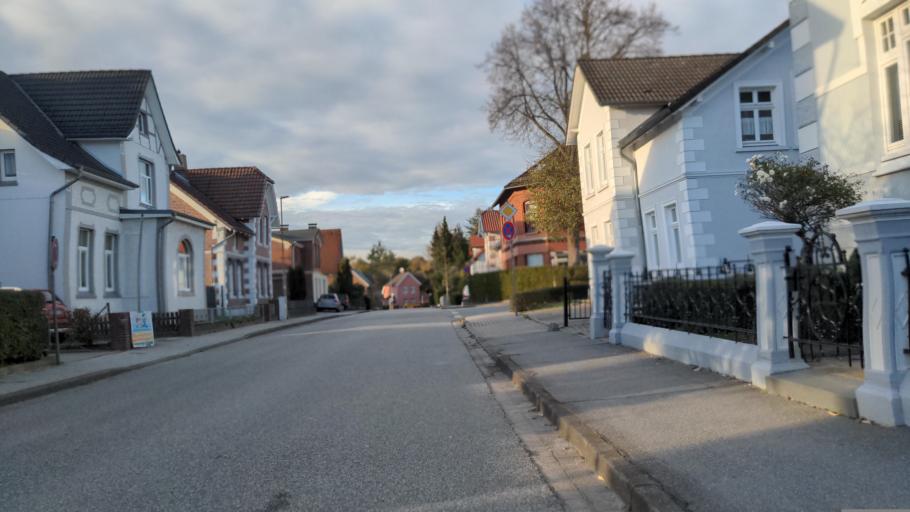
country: DE
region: Schleswig-Holstein
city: Reinfeld
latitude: 53.8331
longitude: 10.4896
